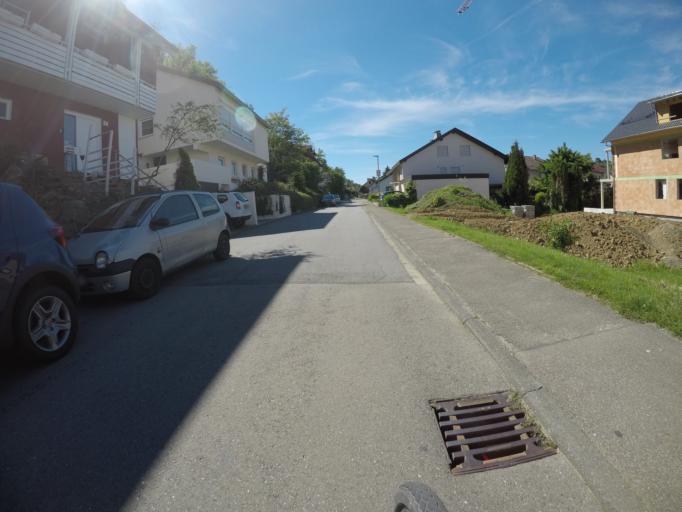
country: DE
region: Baden-Wuerttemberg
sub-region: Karlsruhe Region
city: Konigsbach-Stein
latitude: 48.9503
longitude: 8.6250
